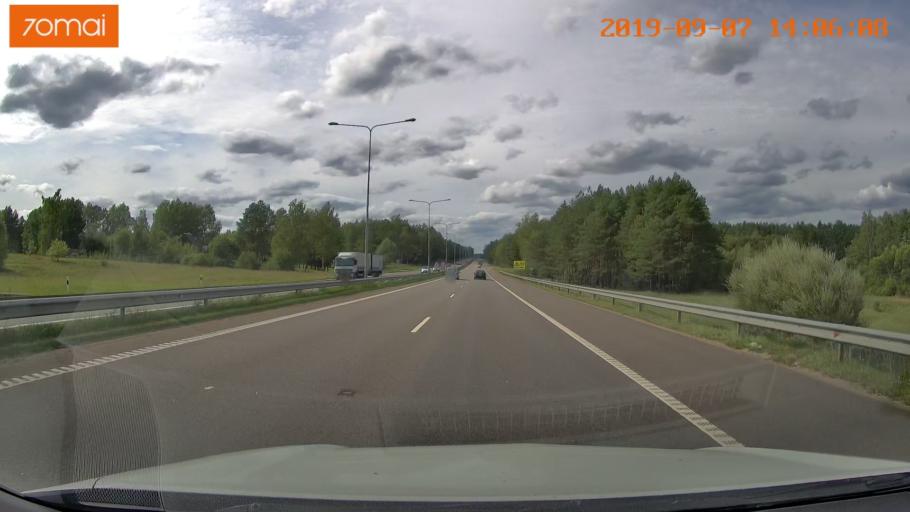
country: LT
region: Vilnius County
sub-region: Vilniaus Rajonas
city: Vievis
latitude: 54.7571
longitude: 24.8937
